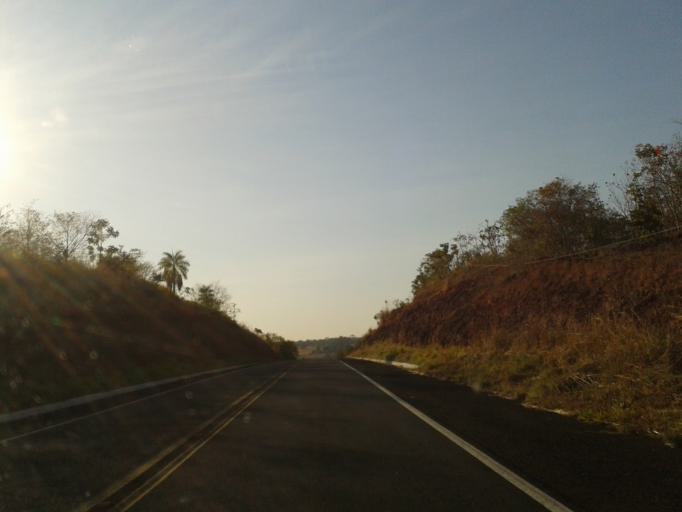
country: BR
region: Minas Gerais
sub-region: Santa Vitoria
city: Santa Vitoria
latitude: -19.1696
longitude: -50.0614
